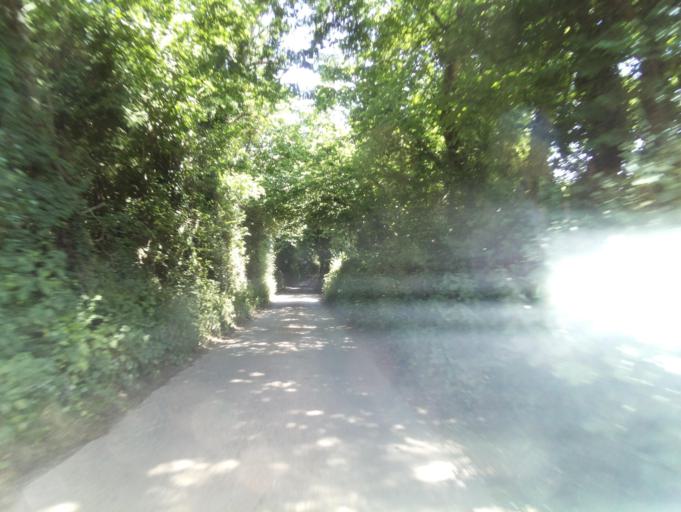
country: GB
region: England
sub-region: Devon
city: Ipplepen
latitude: 50.4995
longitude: -3.6181
